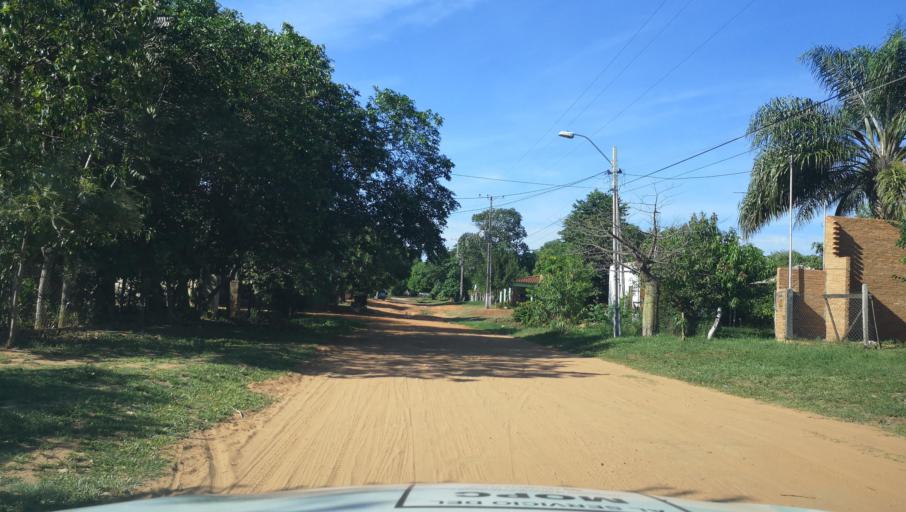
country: PY
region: Misiones
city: Santa Maria
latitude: -26.8754
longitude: -57.0086
